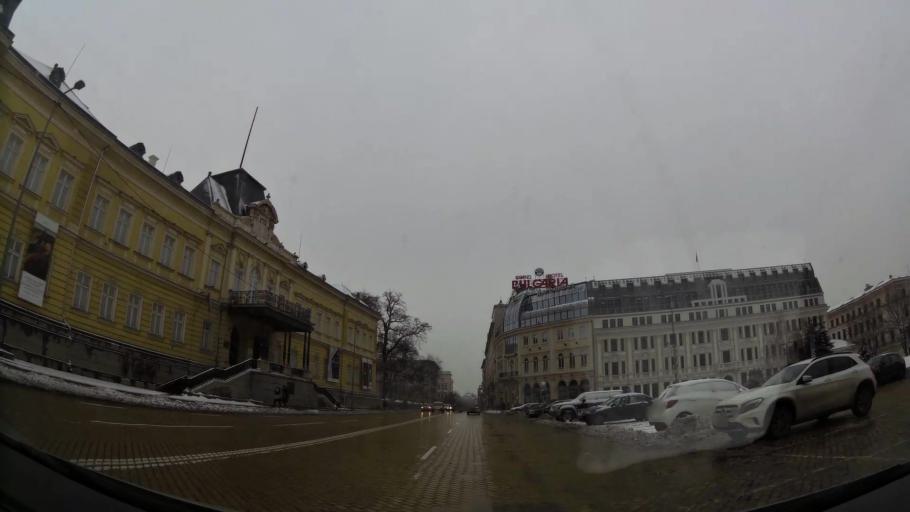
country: BG
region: Sofia-Capital
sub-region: Stolichna Obshtina
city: Sofia
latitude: 42.6961
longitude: 23.3267
